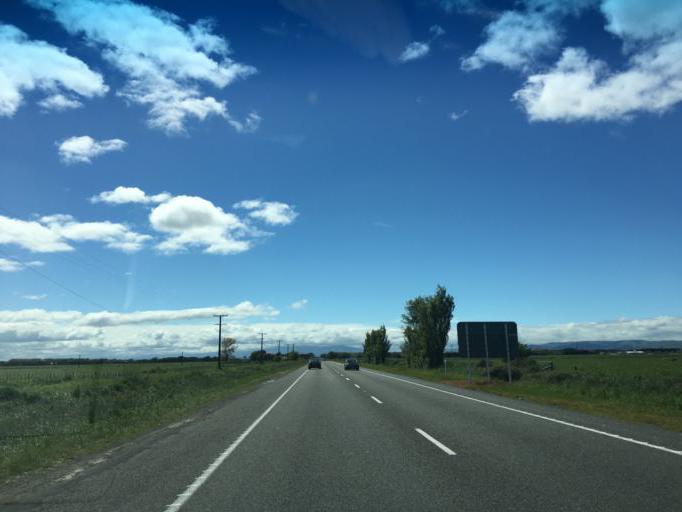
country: NZ
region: Manawatu-Wanganui
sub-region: Palmerston North City
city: Palmerston North
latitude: -40.4096
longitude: 175.4850
